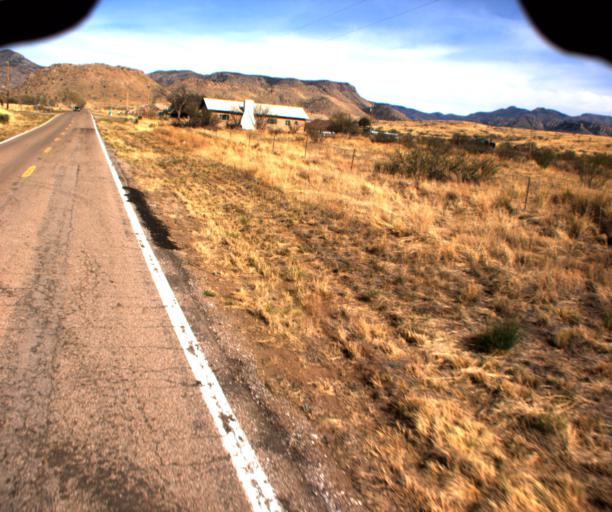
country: US
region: Arizona
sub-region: Cochise County
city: Willcox
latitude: 32.0067
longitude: -109.4076
